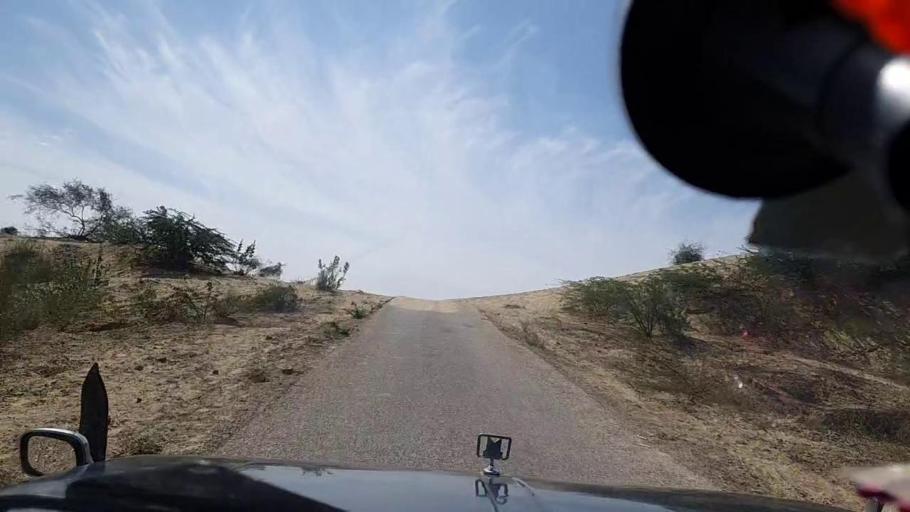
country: PK
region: Sindh
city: Diplo
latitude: 24.3989
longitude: 69.5889
